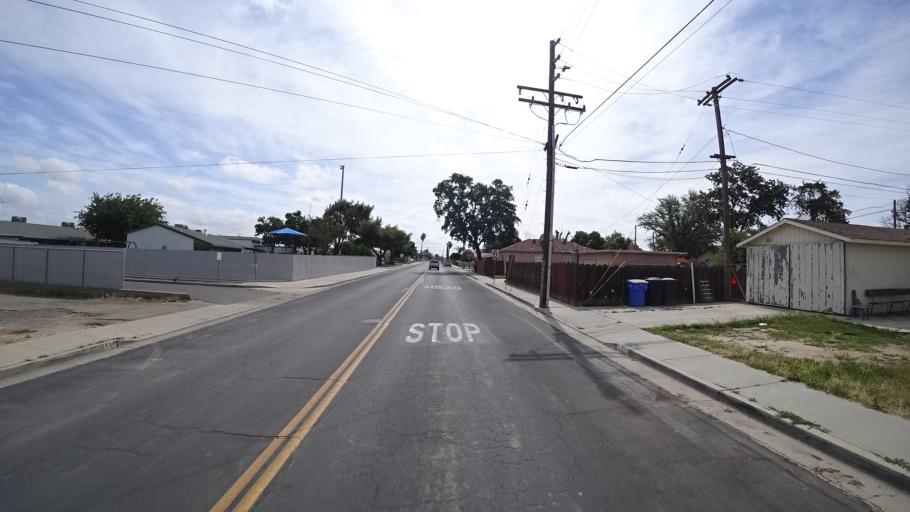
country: US
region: California
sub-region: Kings County
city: Hanford
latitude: 36.3177
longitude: -119.6590
